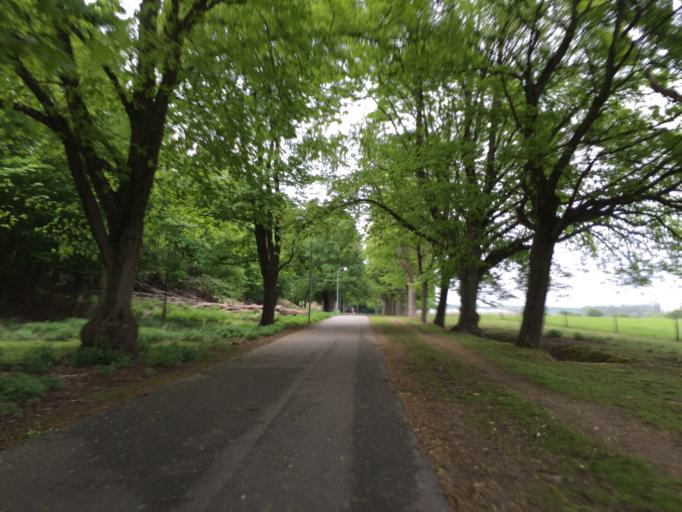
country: DK
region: Capital Region
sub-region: Brondby Kommune
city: Brondbyvester
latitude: 55.6329
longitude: 12.4338
